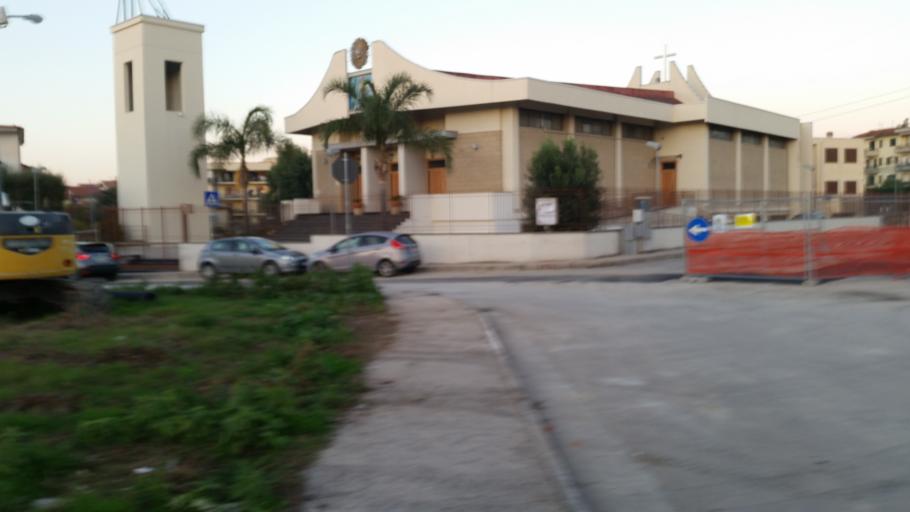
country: IT
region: Campania
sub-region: Provincia di Napoli
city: Mugnano di Napoli
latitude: 40.9076
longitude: 14.2131
